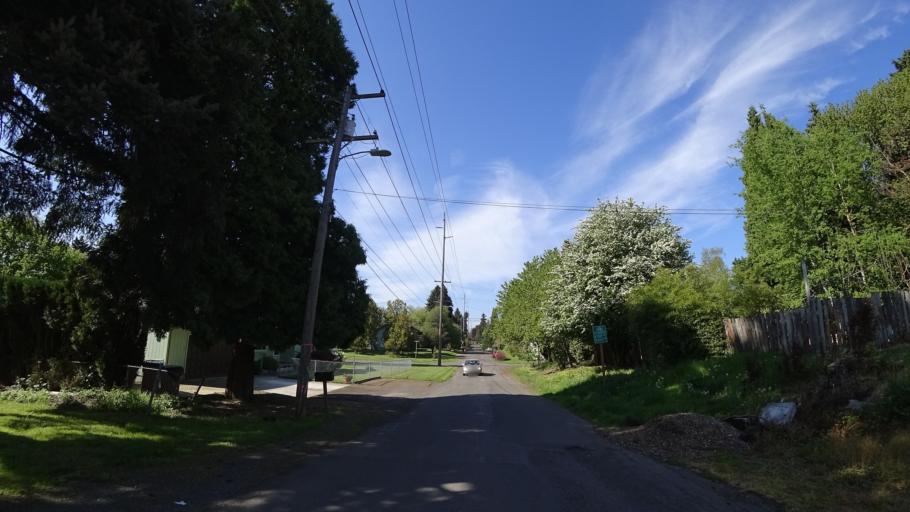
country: US
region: Oregon
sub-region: Clackamas County
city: Milwaukie
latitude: 45.4556
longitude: -122.6327
